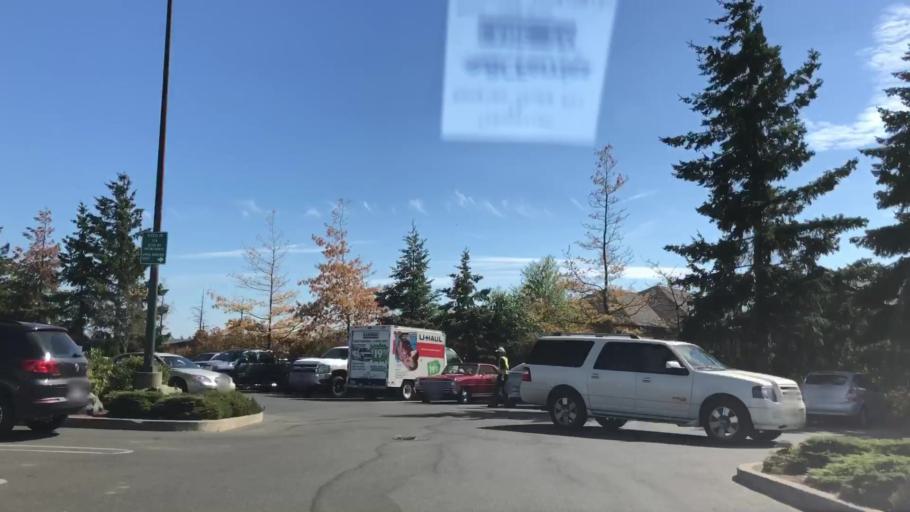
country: CA
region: British Columbia
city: Langford
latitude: 48.4574
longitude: -123.5025
